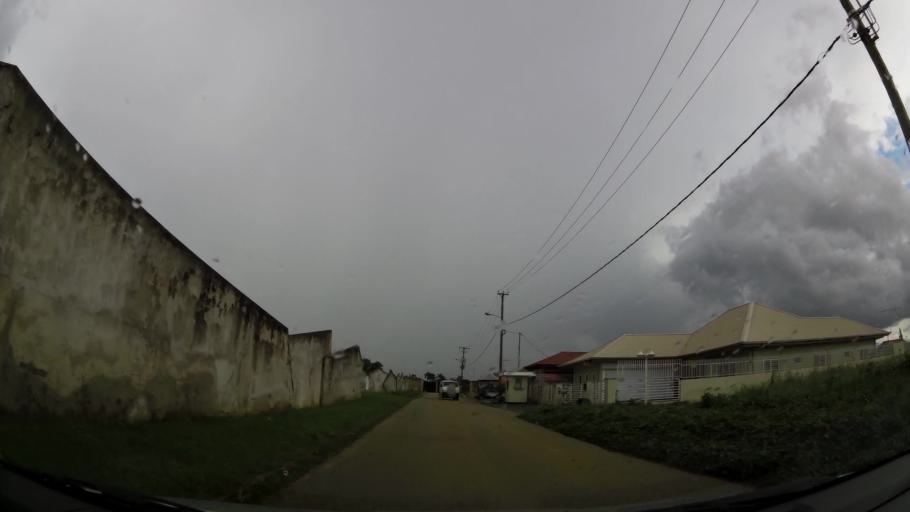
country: SR
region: Commewijne
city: Nieuw Amsterdam
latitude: 5.8506
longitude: -55.1127
